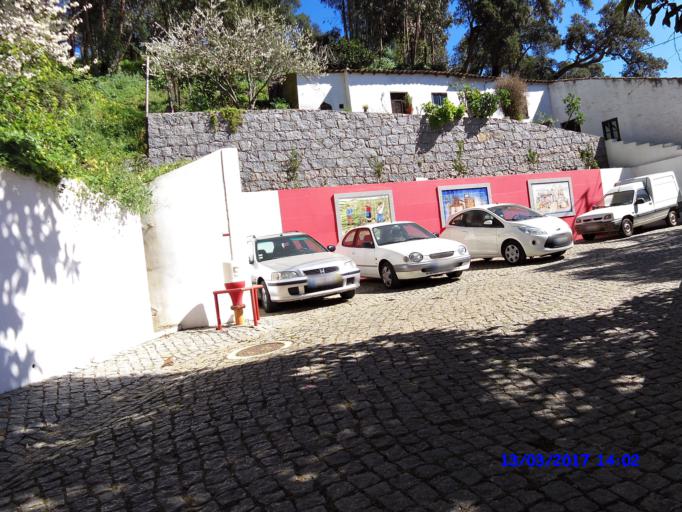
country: PT
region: Faro
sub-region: Monchique
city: Monchique
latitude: 37.3124
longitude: -8.6696
